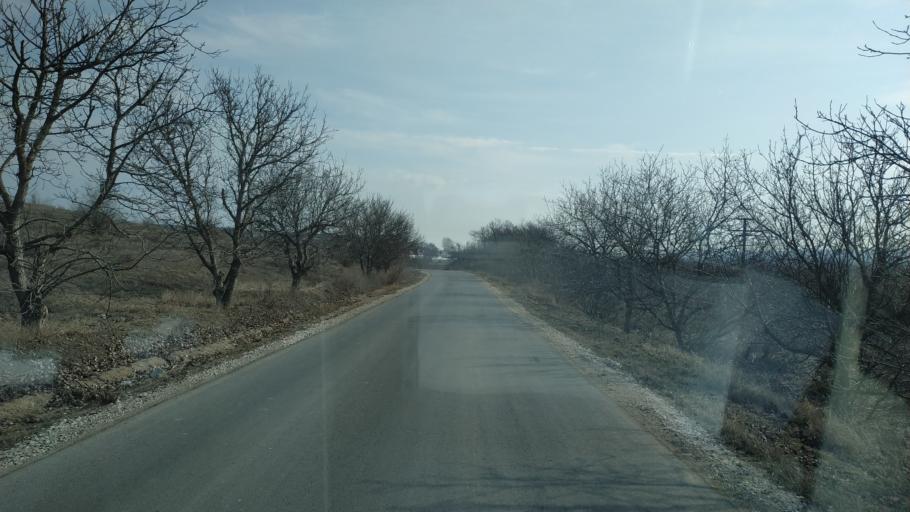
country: MD
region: Chisinau
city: Singera
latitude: 46.9190
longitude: 29.1012
